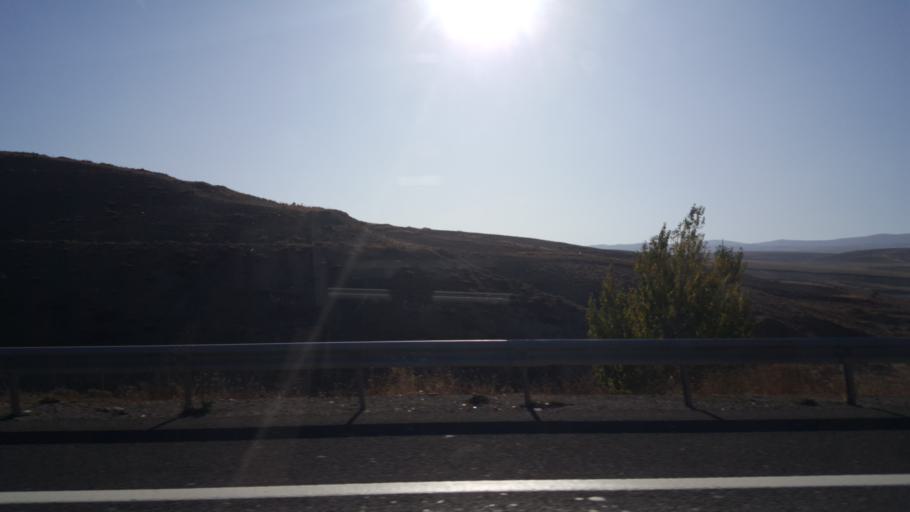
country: TR
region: Ankara
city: Mamak
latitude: 39.8960
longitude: 32.9612
